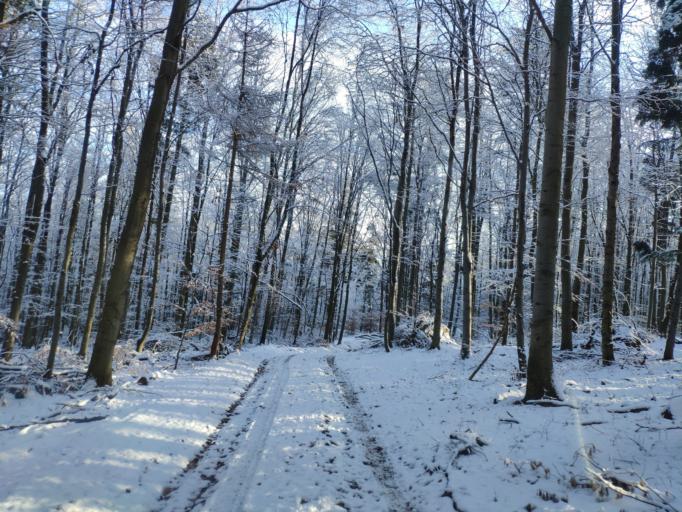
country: SK
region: Kosicky
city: Moldava nad Bodvou
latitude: 48.7446
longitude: 21.0869
